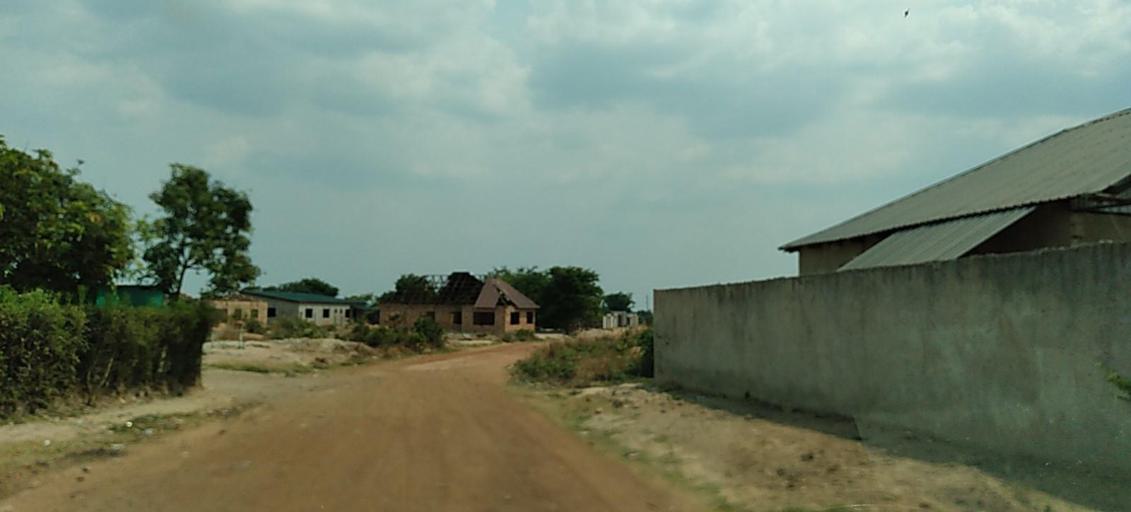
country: ZM
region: Copperbelt
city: Kalulushi
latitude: -12.8566
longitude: 28.0786
